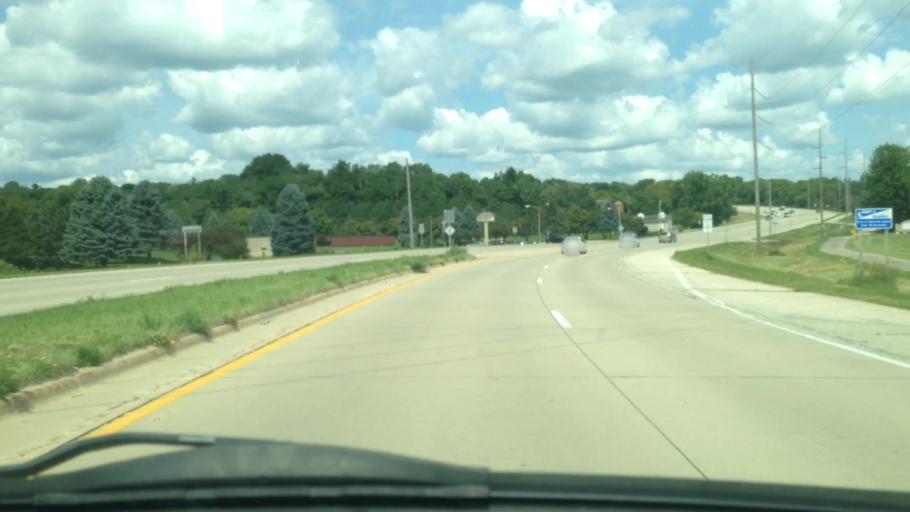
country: US
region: Minnesota
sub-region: Olmsted County
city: Rochester
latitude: 44.0048
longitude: -92.5083
